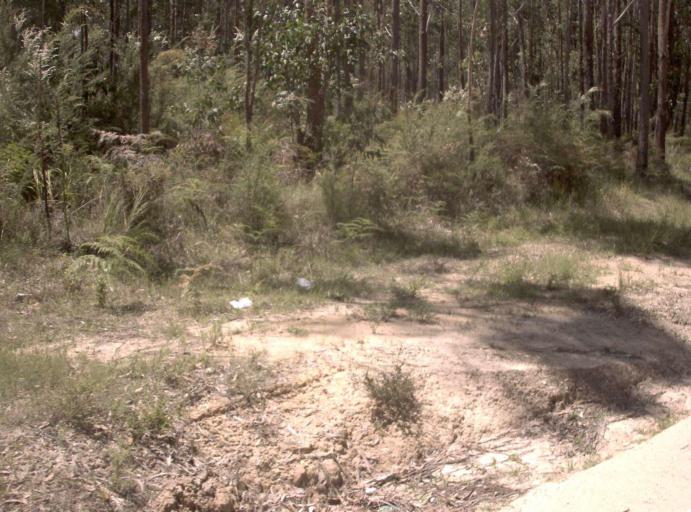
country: AU
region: Victoria
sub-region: East Gippsland
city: Lakes Entrance
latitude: -37.6870
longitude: 148.7562
